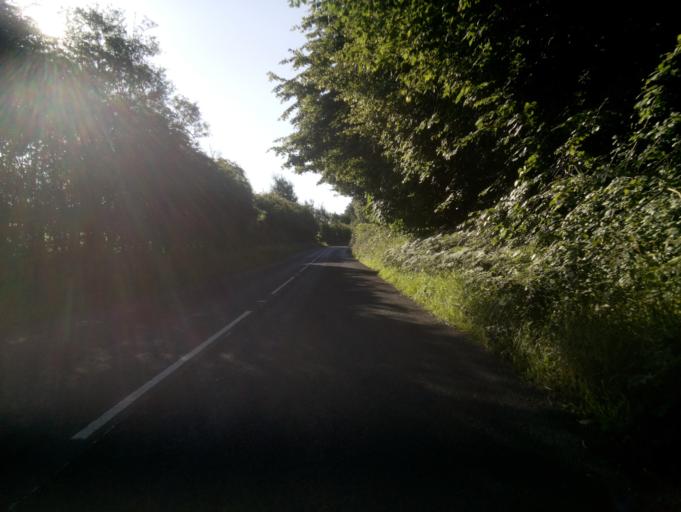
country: GB
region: Wales
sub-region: Monmouthshire
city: Chepstow
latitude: 51.6496
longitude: -2.6991
